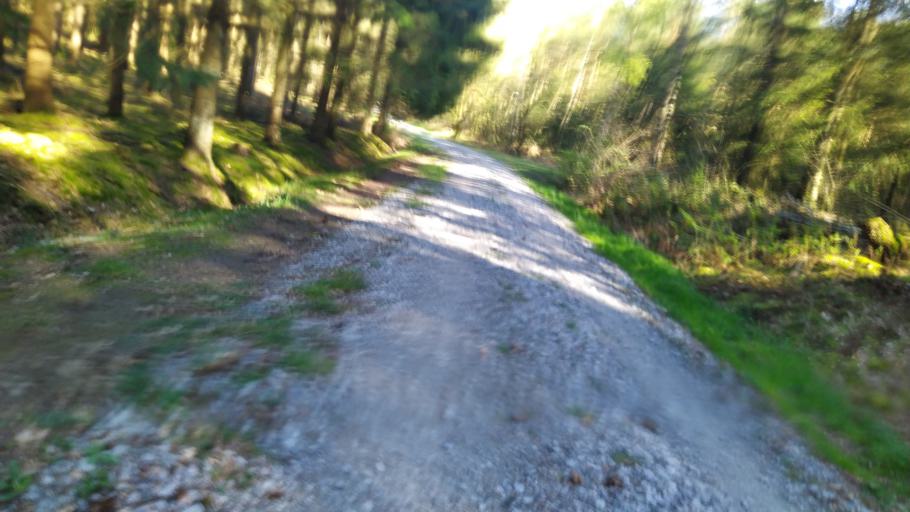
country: DE
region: Lower Saxony
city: Klein Meckelsen
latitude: 53.2942
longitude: 9.4701
